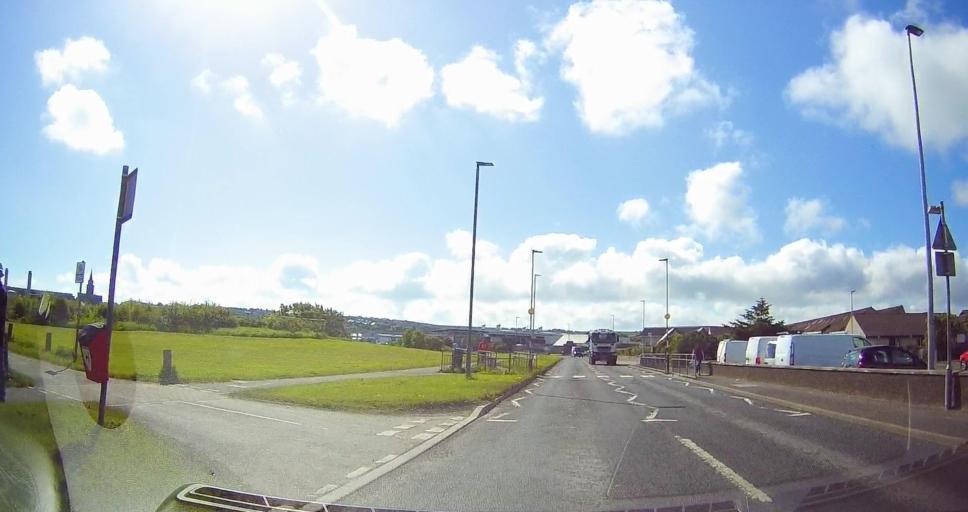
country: GB
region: Scotland
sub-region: Orkney Islands
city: Orkney
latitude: 58.9828
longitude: -2.9705
